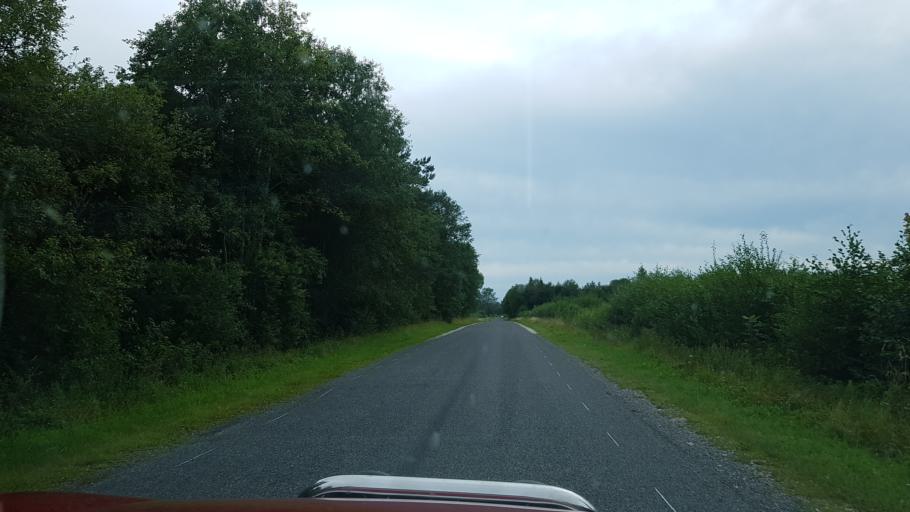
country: EE
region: Laeaene
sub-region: Lihula vald
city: Lihula
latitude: 58.8591
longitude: 23.8181
